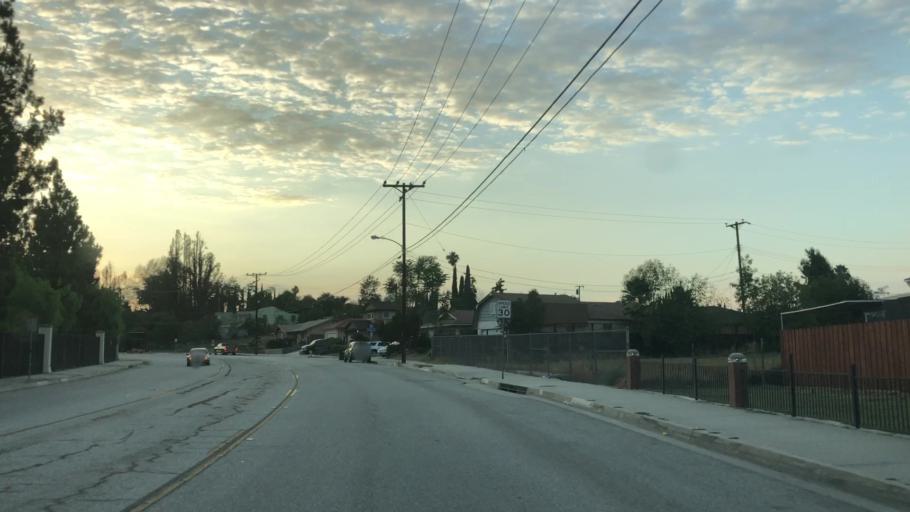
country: US
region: California
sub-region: Los Angeles County
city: South San Gabriel
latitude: 34.0441
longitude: -118.0958
